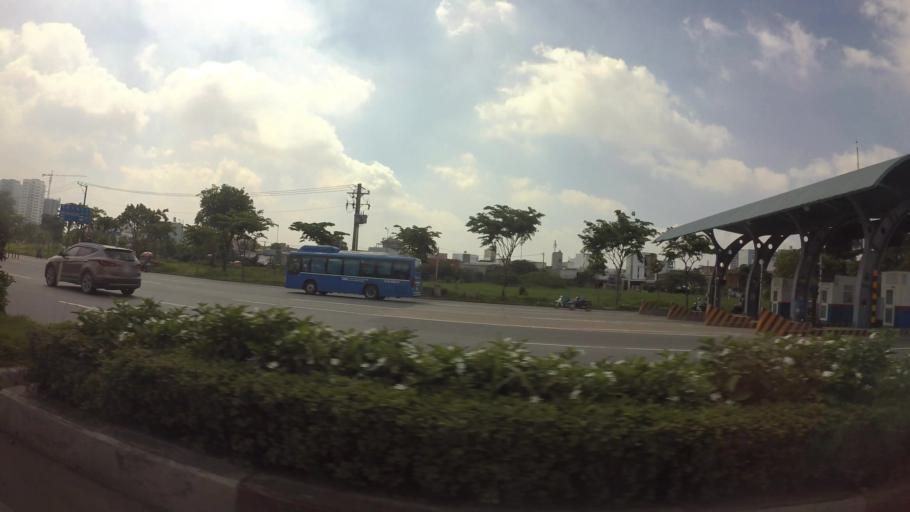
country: VN
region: Ho Chi Minh City
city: Quan Chin
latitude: 10.8215
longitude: 106.7585
